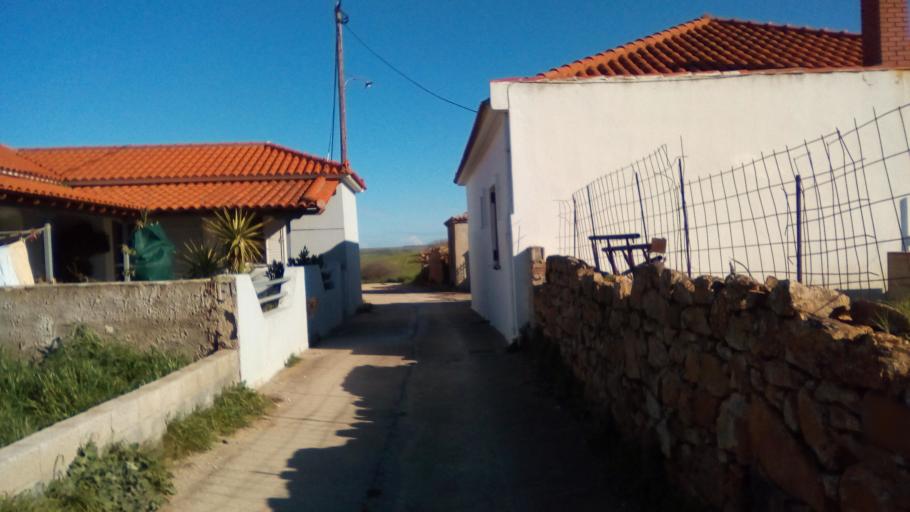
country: GR
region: North Aegean
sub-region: Nomos Lesvou
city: Myrina
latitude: 39.9331
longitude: 25.2328
